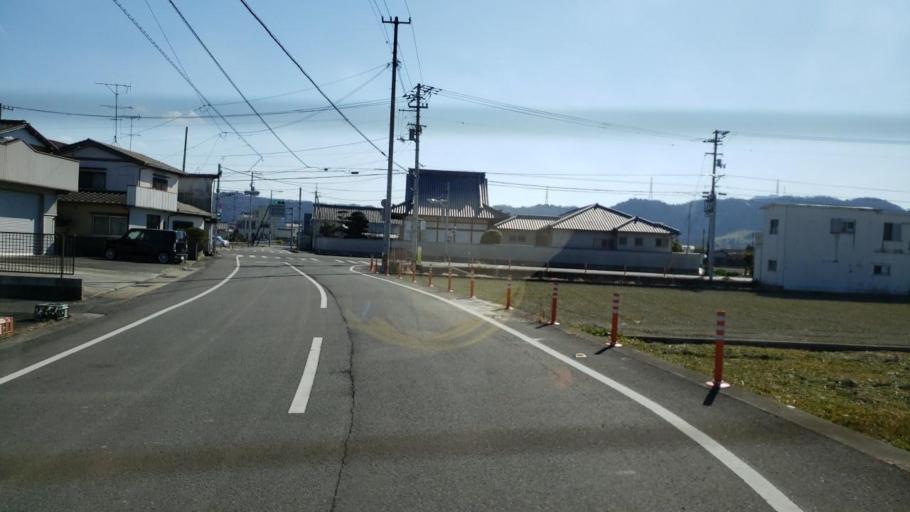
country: JP
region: Tokushima
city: Ishii
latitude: 34.0750
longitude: 134.4296
